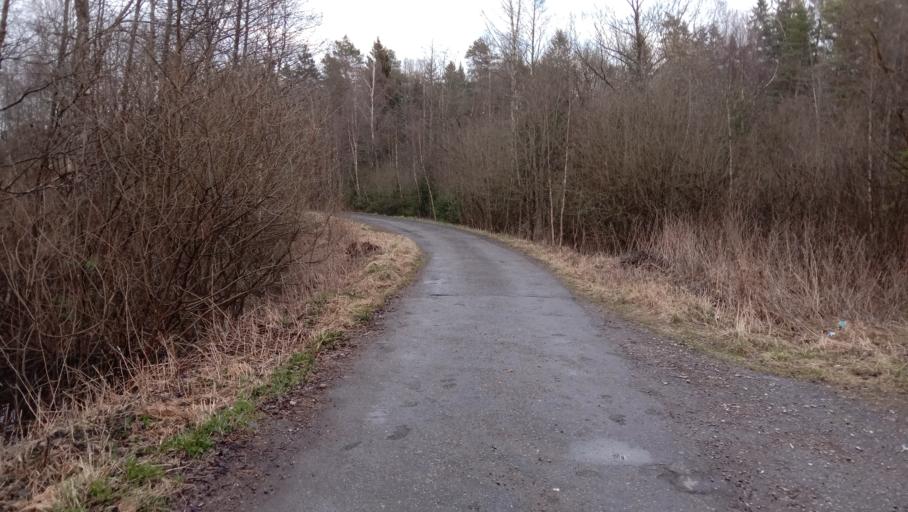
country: RU
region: Moskovskaya
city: Uvarovka
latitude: 55.7641
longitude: 35.7912
